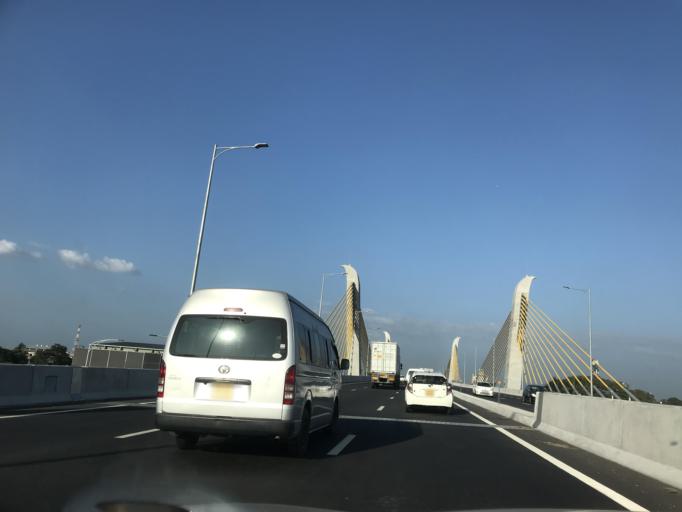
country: LK
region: Western
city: Peliyagoda
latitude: 6.9533
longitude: 79.8813
